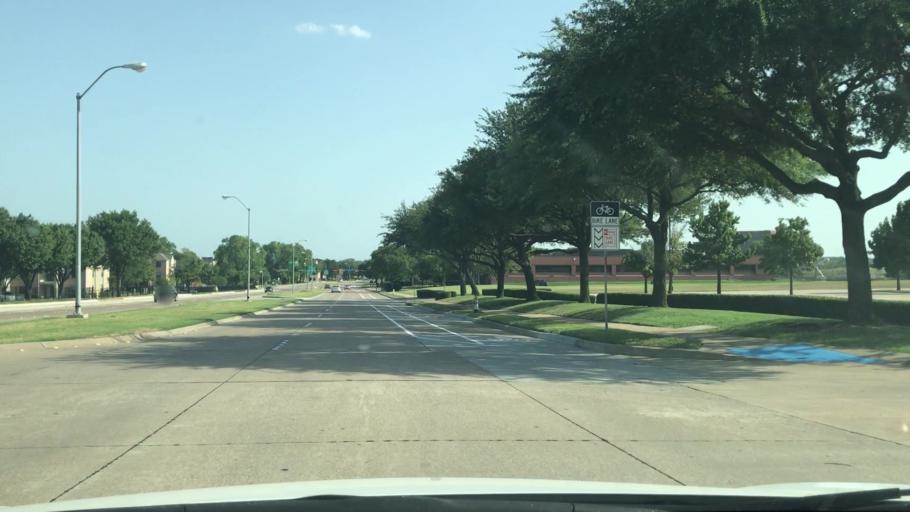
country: US
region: Texas
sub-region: Dallas County
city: Richardson
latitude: 32.9882
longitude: -96.7565
